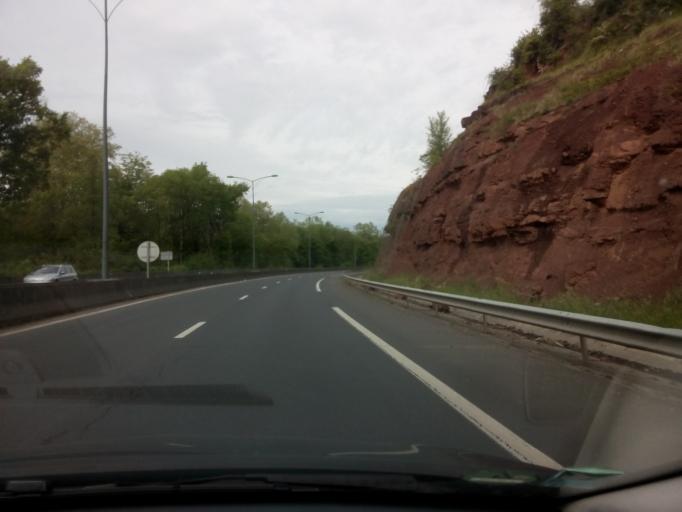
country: FR
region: Limousin
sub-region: Departement de la Correze
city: Saint-Pantaleon-de-Larche
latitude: 45.1645
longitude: 1.4738
